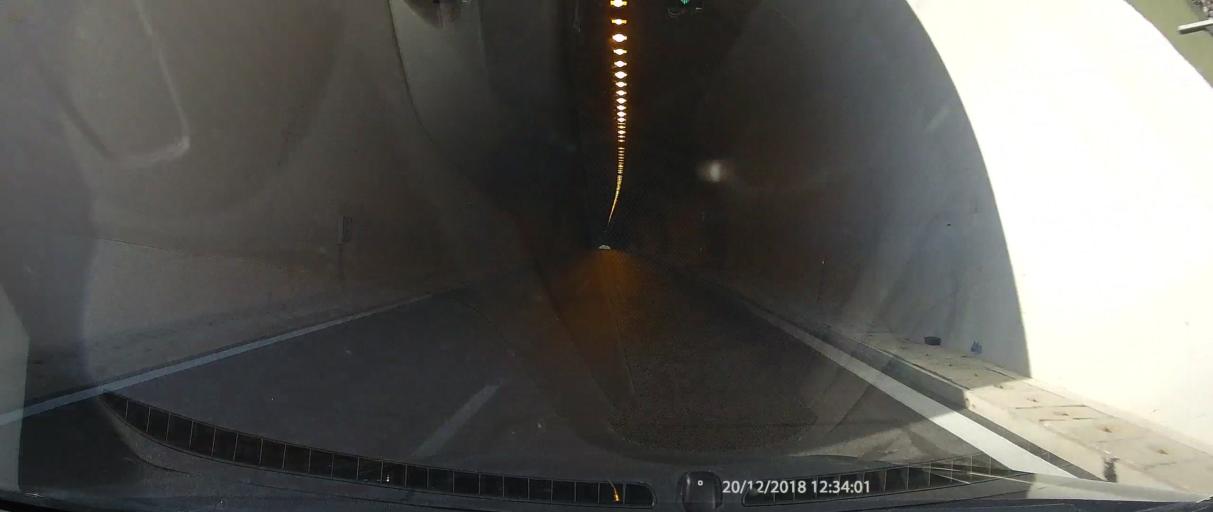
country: GR
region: West Greece
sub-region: Nomos Aitolias kai Akarnanias
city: Antirrio
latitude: 38.3530
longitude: 21.7262
